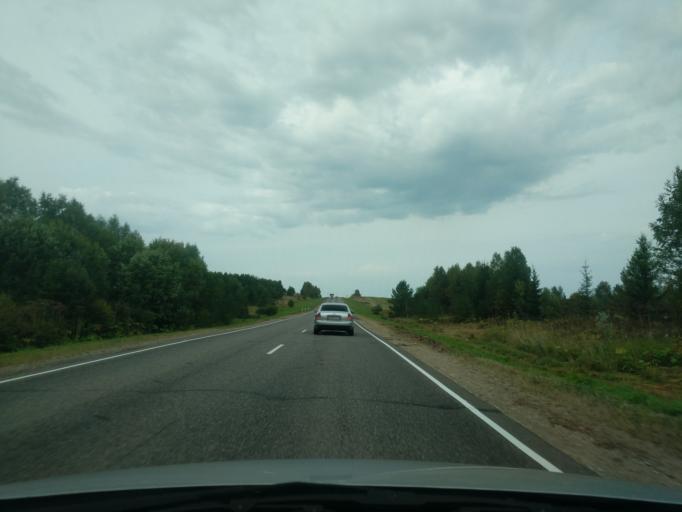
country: RU
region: Kirov
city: Mirnyy
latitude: 58.2730
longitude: 47.7798
